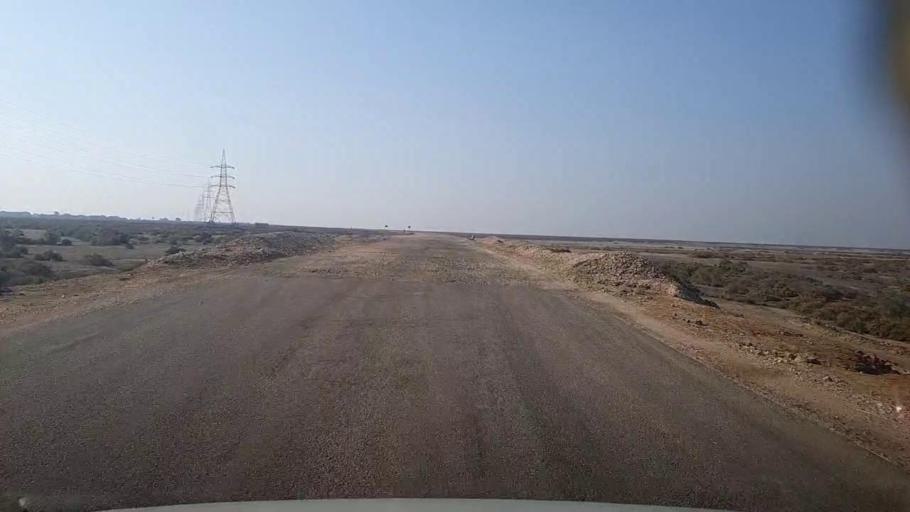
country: PK
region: Sindh
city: Gharo
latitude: 24.6310
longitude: 67.4979
